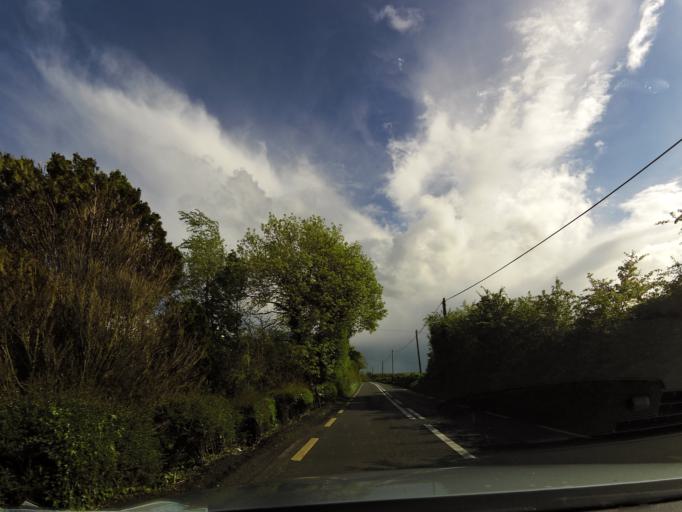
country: IE
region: Munster
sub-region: North Tipperary
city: Templemore
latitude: 52.7847
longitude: -7.8432
